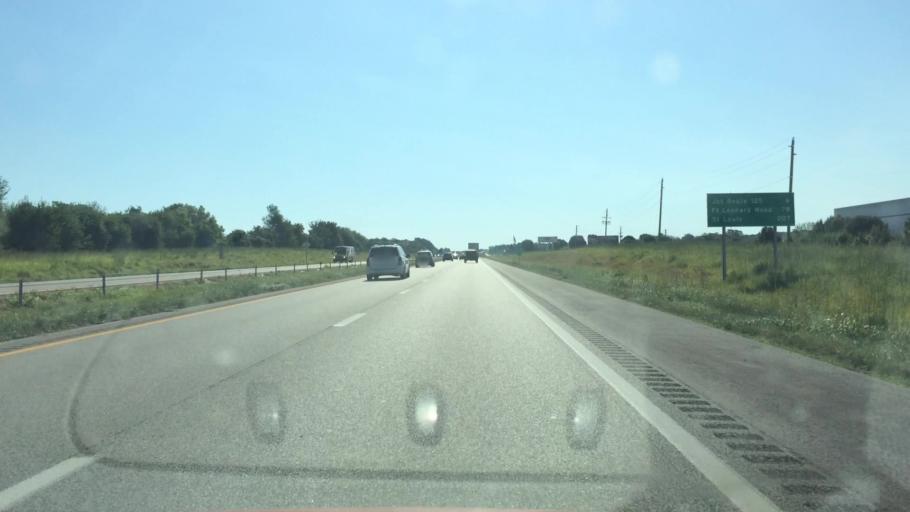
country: US
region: Missouri
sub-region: Greene County
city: Strafford
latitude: 37.2501
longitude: -93.2095
